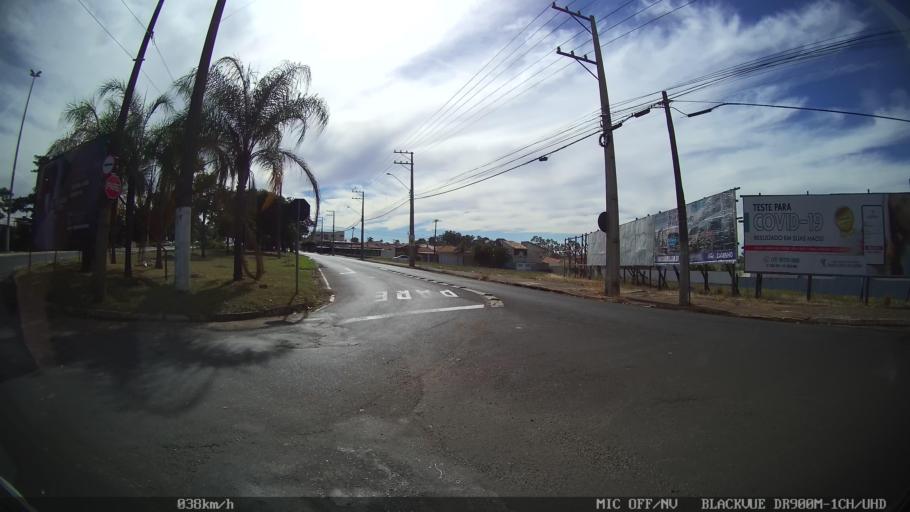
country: BR
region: Sao Paulo
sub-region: Catanduva
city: Catanduva
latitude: -21.1160
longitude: -48.9637
